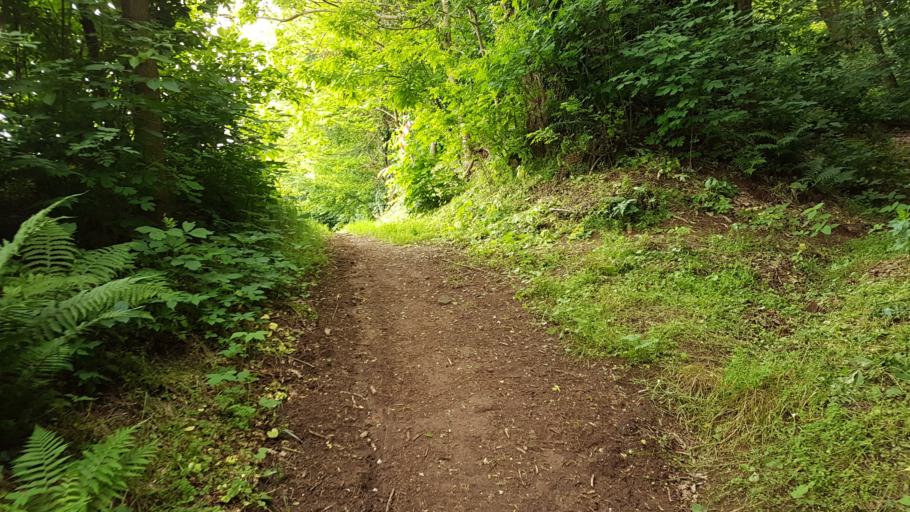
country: IT
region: Veneto
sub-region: Provincia di Vicenza
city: Nogarole Vicentino
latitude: 45.5589
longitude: 11.3168
